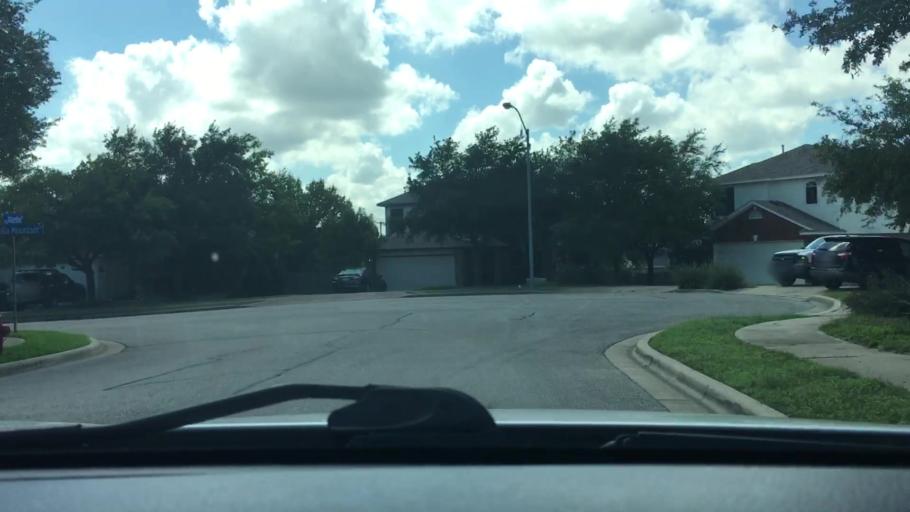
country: US
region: Texas
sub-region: Travis County
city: Windemere
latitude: 30.4735
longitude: -97.6530
